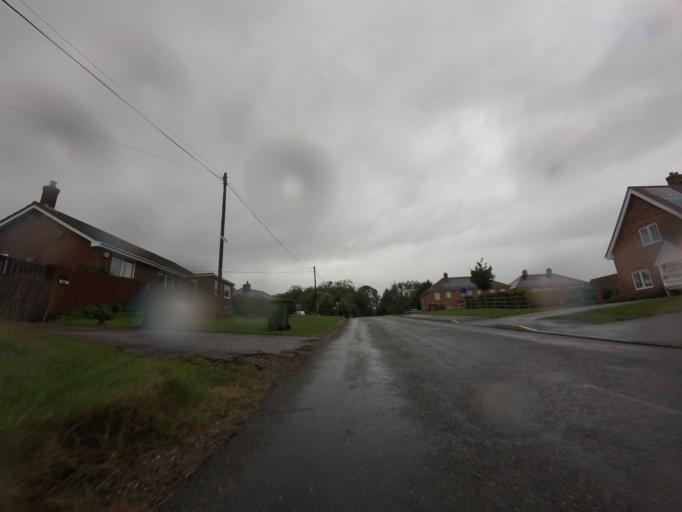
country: GB
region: England
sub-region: Cambridgeshire
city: Wimpole
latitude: 52.1872
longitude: -0.0603
